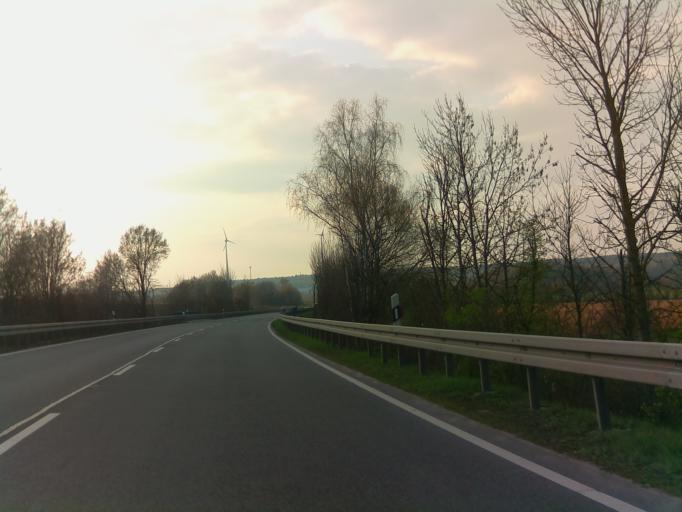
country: DE
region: Hesse
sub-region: Regierungsbezirk Kassel
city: Friedewald
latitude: 50.8779
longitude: 9.8888
